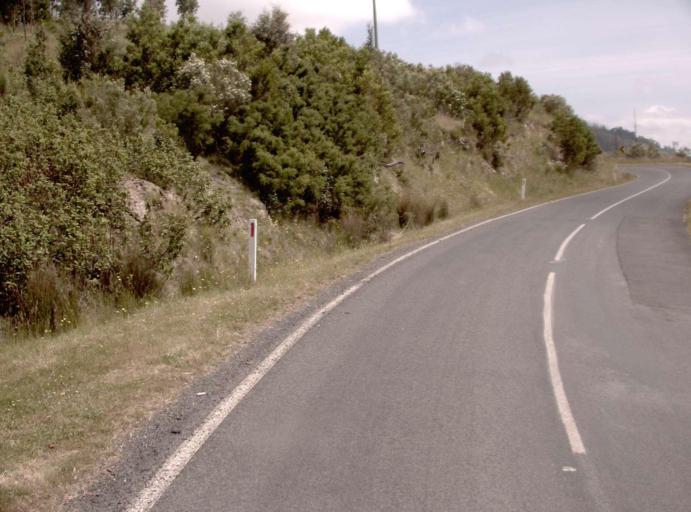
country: AU
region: Victoria
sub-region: Latrobe
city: Traralgon
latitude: -38.3749
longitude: 146.5693
